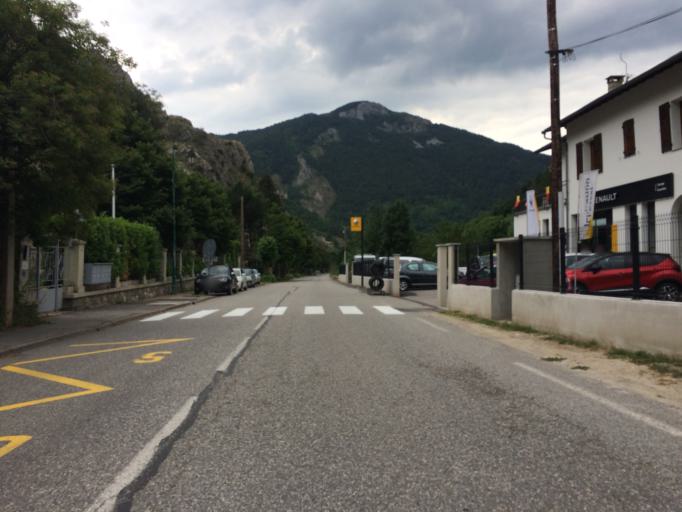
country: FR
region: Provence-Alpes-Cote d'Azur
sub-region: Departement des Alpes-Maritimes
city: Tende
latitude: 44.0829
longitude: 7.5952
